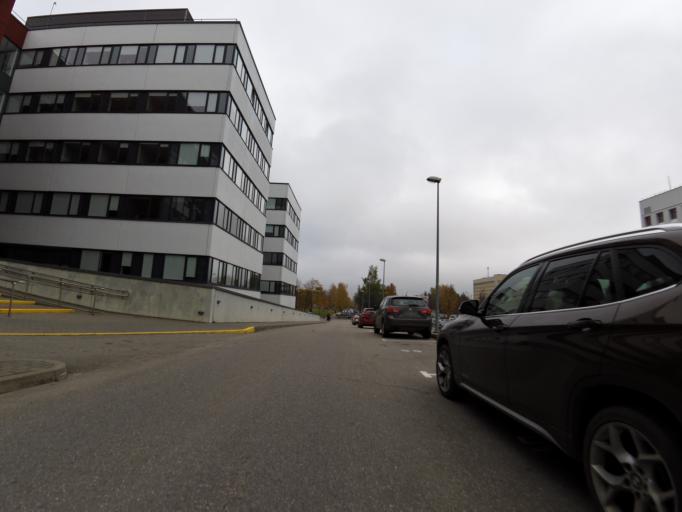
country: LT
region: Vilnius County
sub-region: Vilnius
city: Fabijoniskes
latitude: 54.7534
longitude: 25.2786
